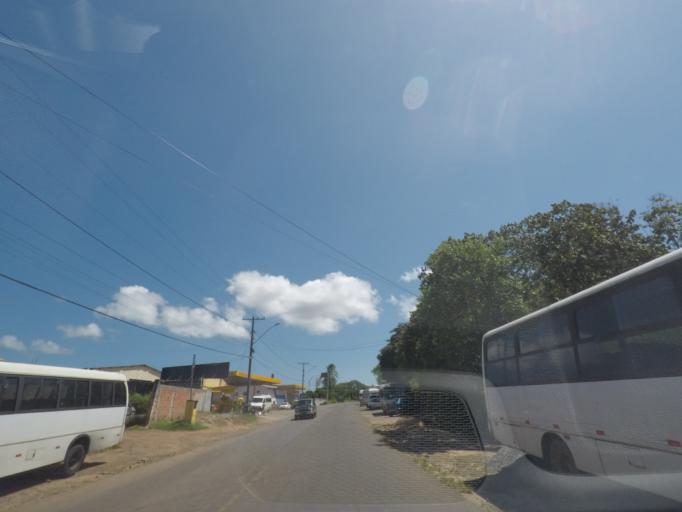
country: BR
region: Bahia
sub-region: Valenca
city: Valenca
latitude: -13.3782
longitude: -39.0743
